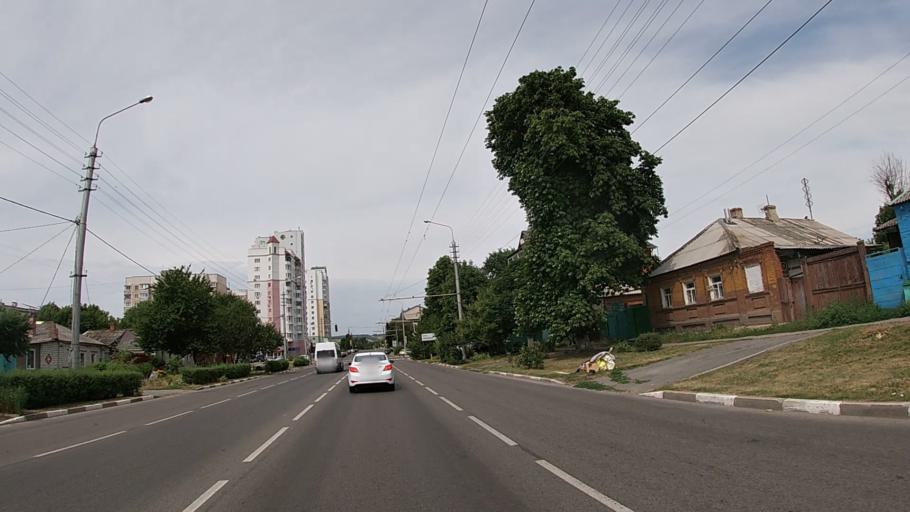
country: RU
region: Belgorod
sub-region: Belgorodskiy Rayon
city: Belgorod
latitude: 50.6011
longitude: 36.5719
